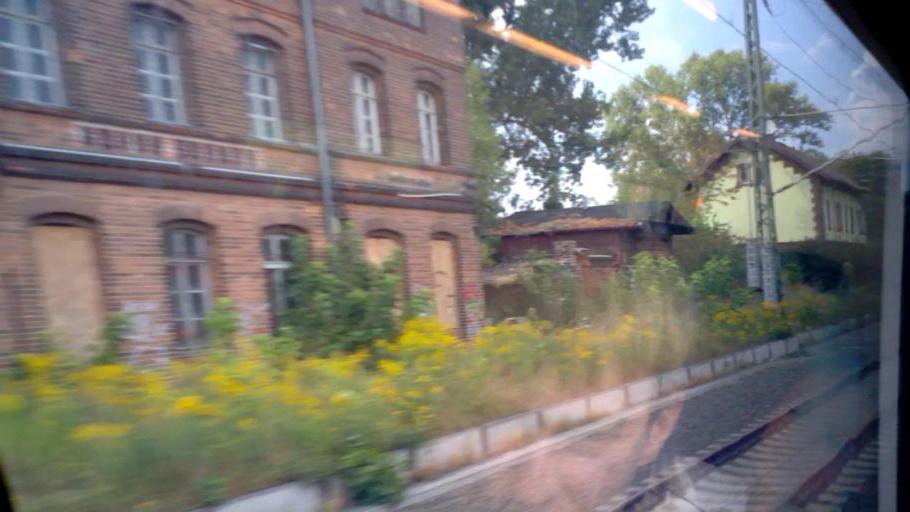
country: DE
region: Brandenburg
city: Grossbeeren
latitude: 52.3521
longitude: 13.2852
